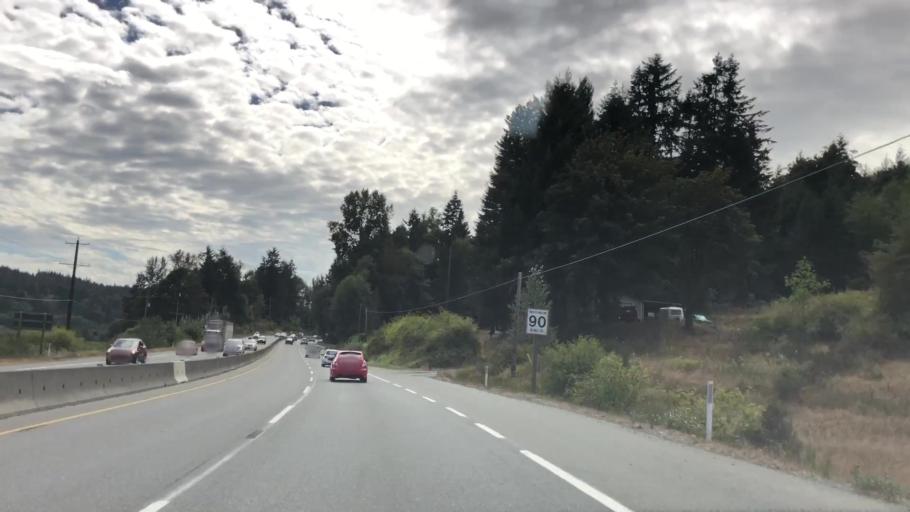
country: CA
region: British Columbia
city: North Cowichan
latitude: 48.8699
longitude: -123.7113
